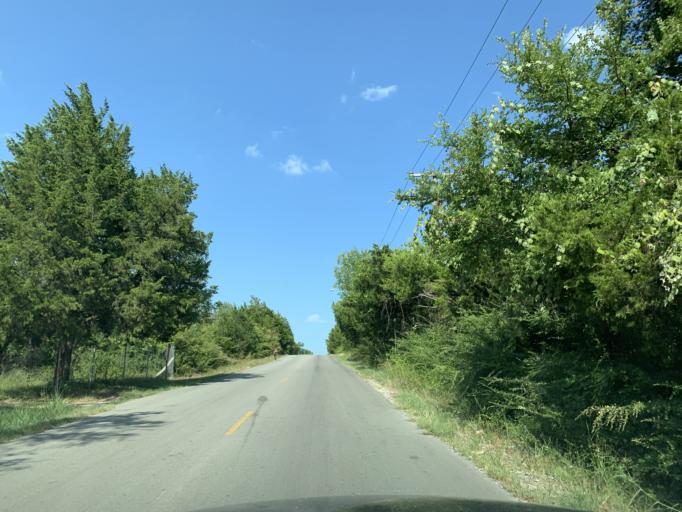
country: US
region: Texas
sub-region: Dallas County
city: Hutchins
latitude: 32.6761
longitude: -96.7702
